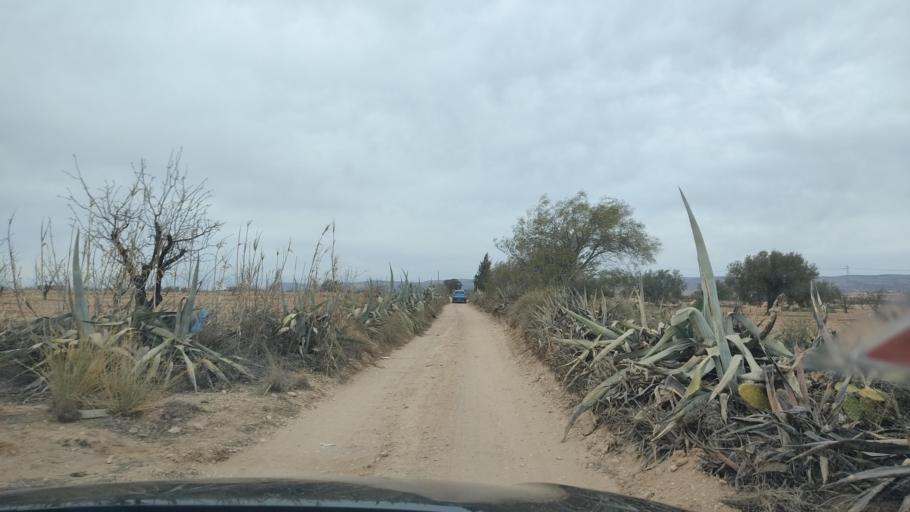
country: TN
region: Al Qasrayn
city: Kasserine
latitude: 35.2261
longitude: 8.9338
